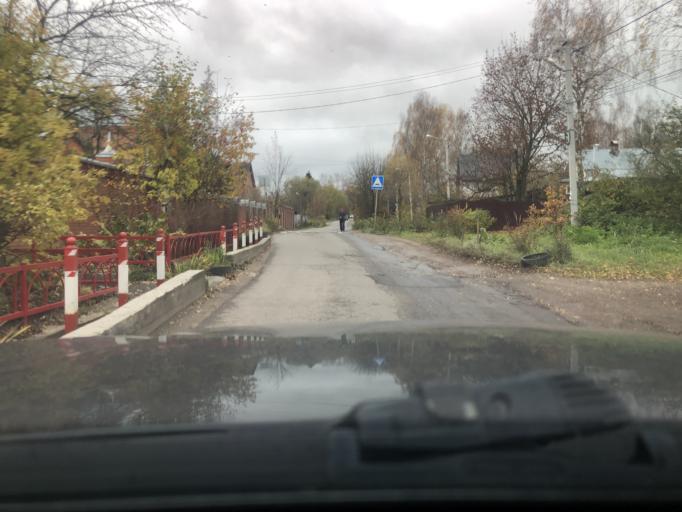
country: RU
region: Moskovskaya
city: Sergiyev Posad
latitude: 56.2980
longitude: 38.1121
